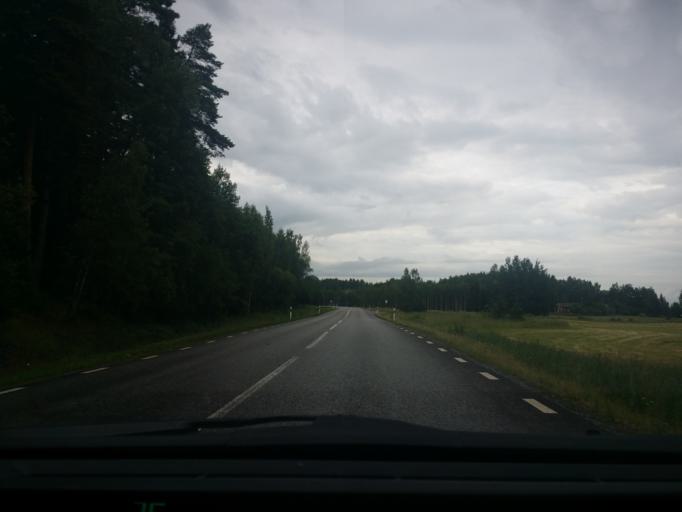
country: SE
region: OErebro
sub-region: Lindesbergs Kommun
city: Frovi
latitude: 59.4513
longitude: 15.3168
